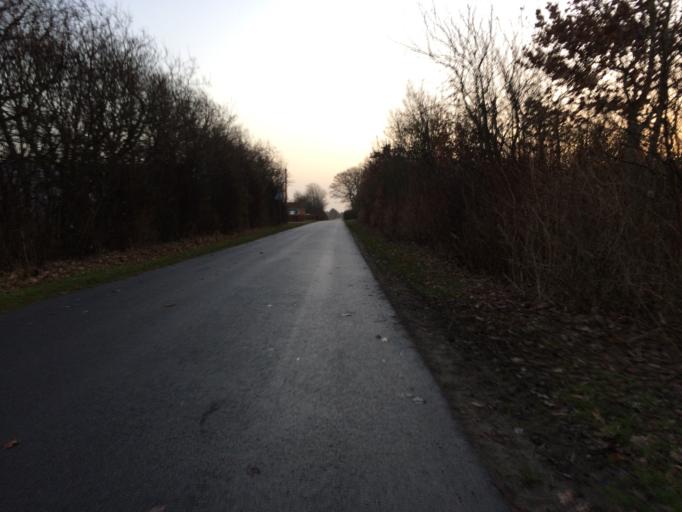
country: DK
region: Central Jutland
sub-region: Holstebro Kommune
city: Ulfborg
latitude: 56.2762
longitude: 8.2907
